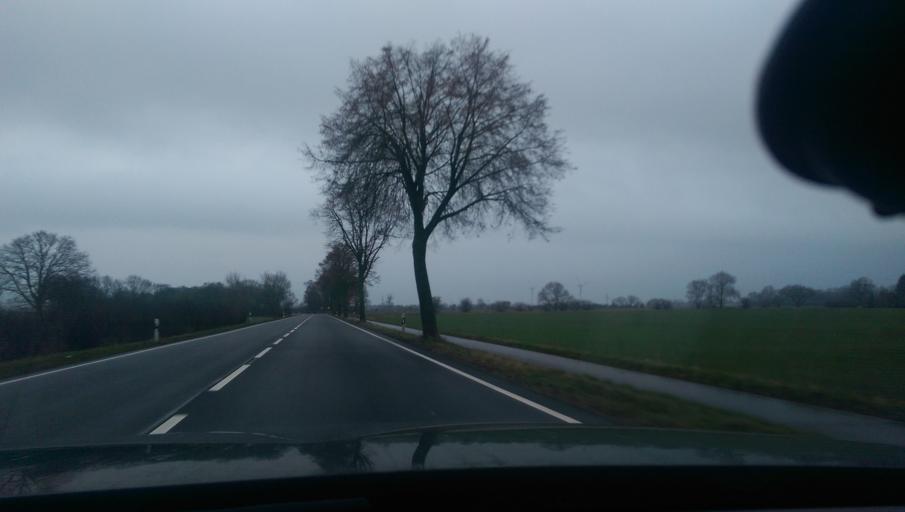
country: DE
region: Lower Saxony
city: Verden
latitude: 52.9017
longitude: 9.2170
